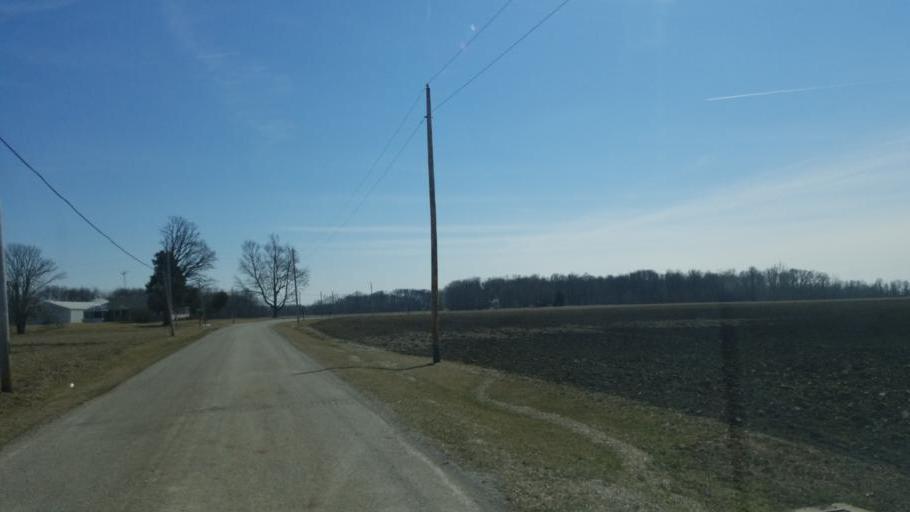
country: US
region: Ohio
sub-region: Crawford County
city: Bucyrus
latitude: 40.6651
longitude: -82.9679
